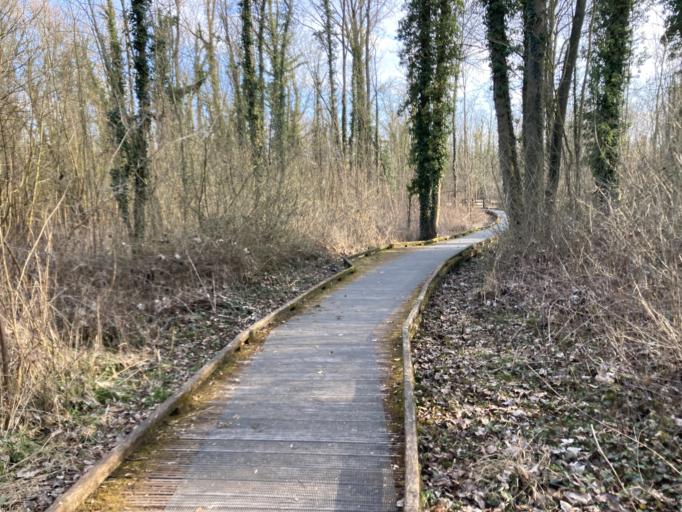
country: FR
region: Nord-Pas-de-Calais
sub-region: Departement du Pas-de-Calais
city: Annequin
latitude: 50.5225
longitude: 2.7085
